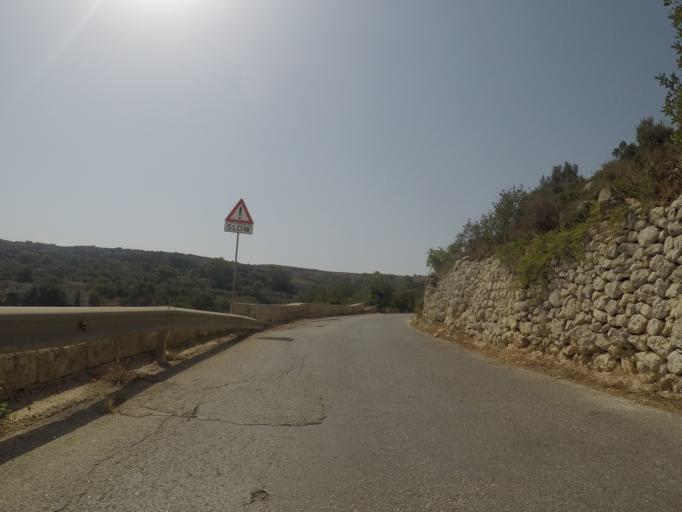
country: MT
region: L-Imgarr
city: Imgarr
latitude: 35.9375
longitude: 14.3800
